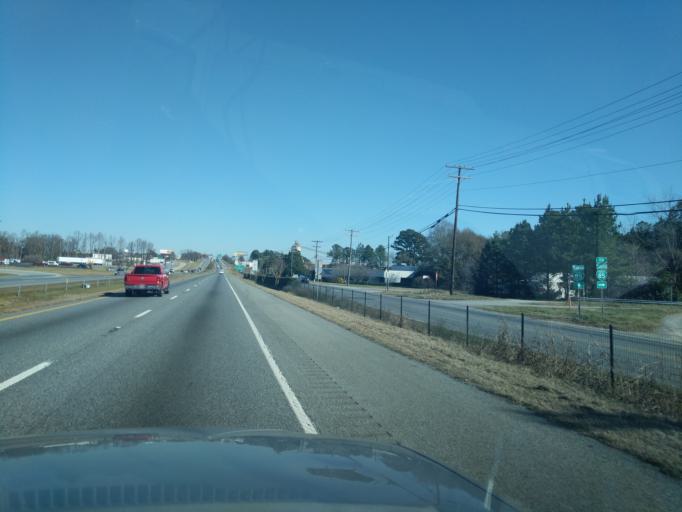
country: US
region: South Carolina
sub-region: Spartanburg County
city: Southern Shops
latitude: 34.9750
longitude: -81.9844
